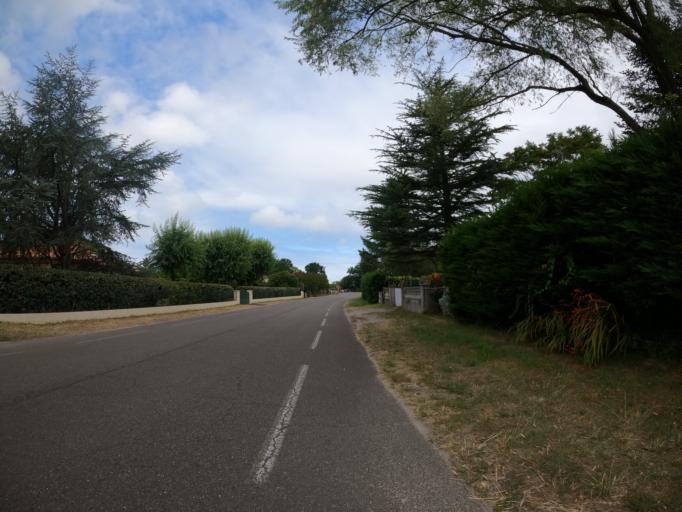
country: FR
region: Aquitaine
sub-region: Departement des Landes
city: Leon
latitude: 43.8803
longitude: -1.3048
